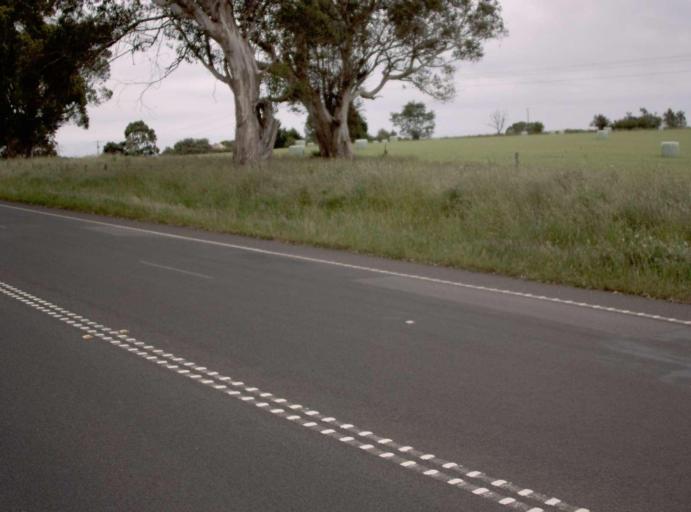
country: AU
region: Victoria
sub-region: Baw Baw
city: Warragul
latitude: -38.4588
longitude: 145.9313
